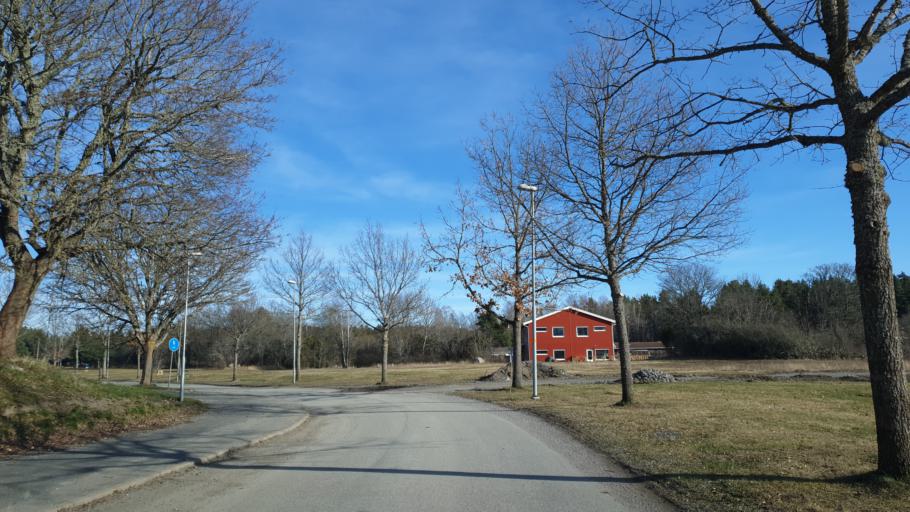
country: SE
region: Uppsala
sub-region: Enkopings Kommun
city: Grillby
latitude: 59.5573
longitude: 17.2451
